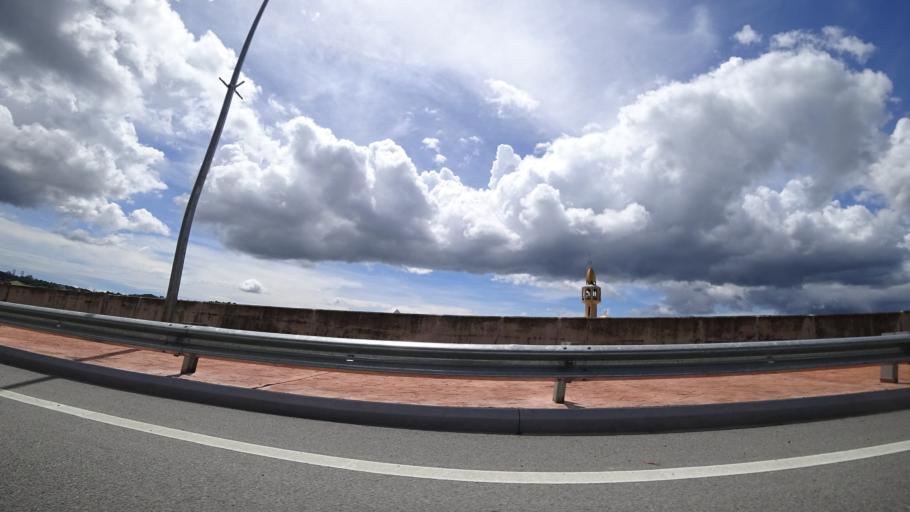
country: BN
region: Brunei and Muara
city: Bandar Seri Begawan
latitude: 4.8788
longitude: 114.9441
